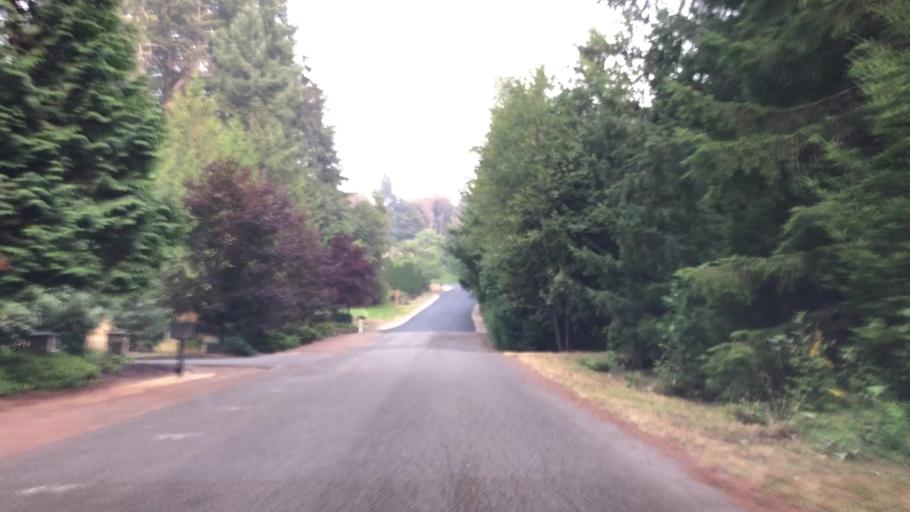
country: US
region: Washington
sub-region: King County
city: Cottage Lake
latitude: 47.7298
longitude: -122.0978
